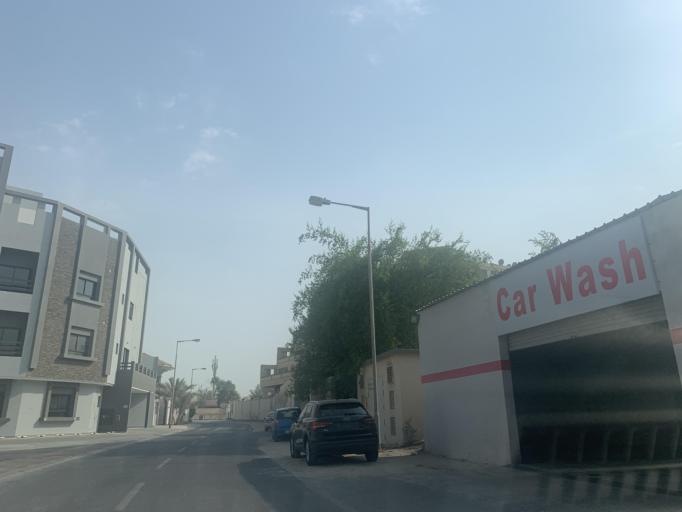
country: BH
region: Manama
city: Jidd Hafs
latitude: 26.2191
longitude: 50.4964
